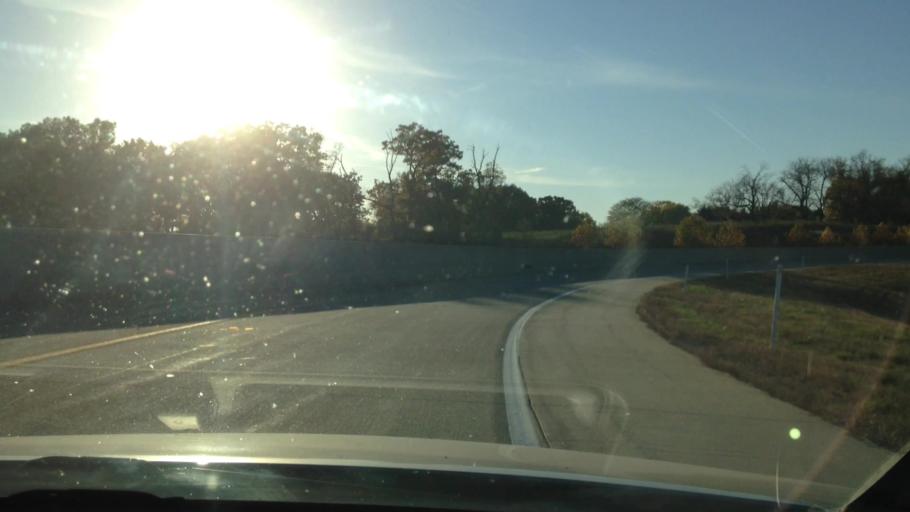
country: US
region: Kansas
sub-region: Leavenworth County
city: Basehor
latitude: 39.1137
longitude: -94.8949
